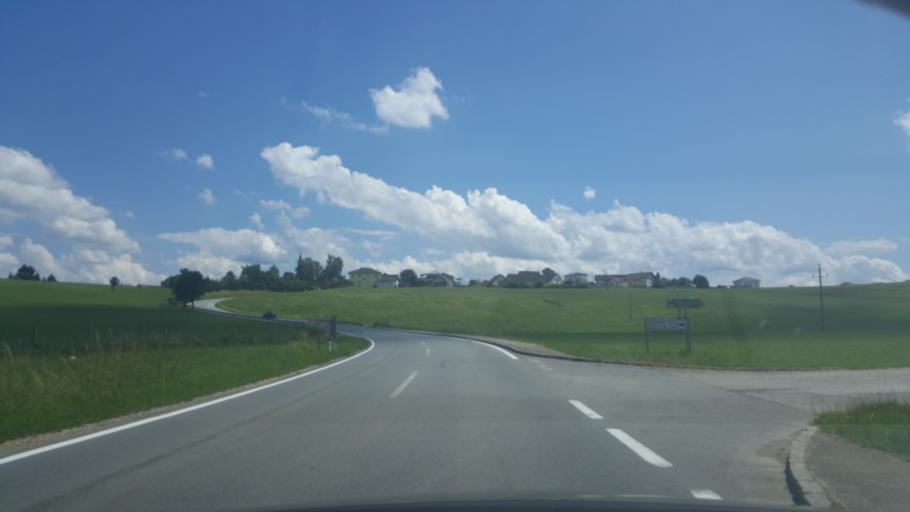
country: AT
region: Upper Austria
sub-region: Politischer Bezirk Vocklabruck
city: Gampern
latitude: 47.9932
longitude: 13.5483
